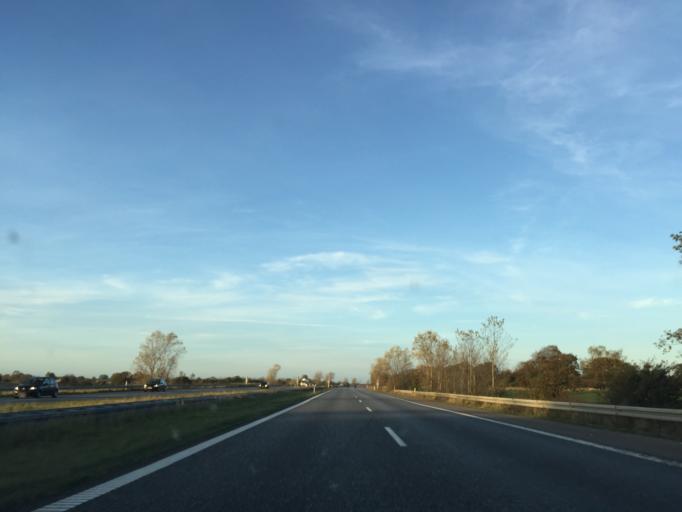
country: DK
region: South Denmark
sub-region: Kolding Kommune
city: Christiansfeld
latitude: 55.4095
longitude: 9.4551
